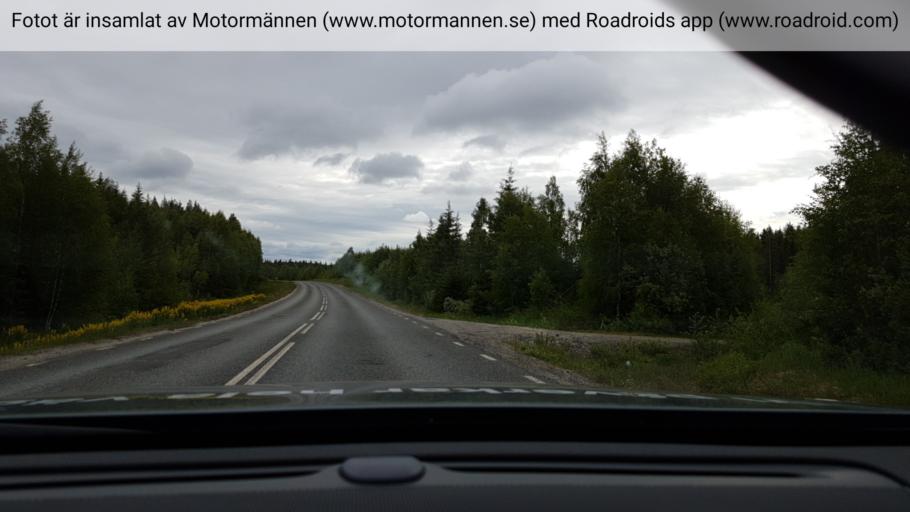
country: SE
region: Vaesterbotten
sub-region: Lycksele Kommun
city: Lycksele
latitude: 64.5157
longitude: 18.4119
